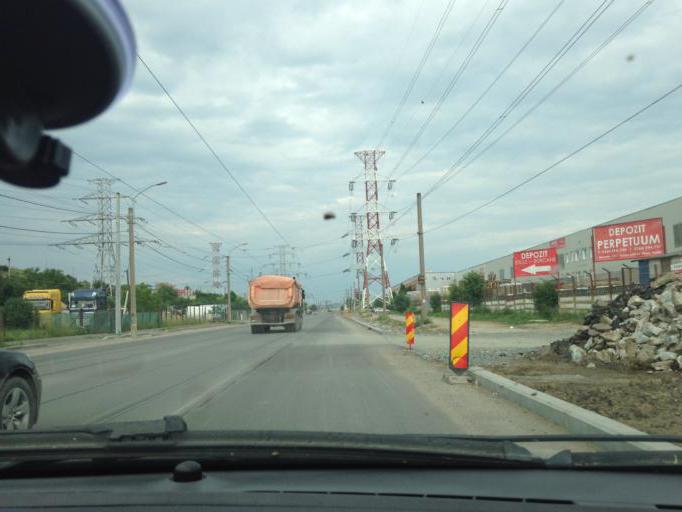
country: RO
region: Cluj
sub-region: Municipiul Cluj-Napoca
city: Cluj-Napoca
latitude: 46.7961
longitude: 23.6398
